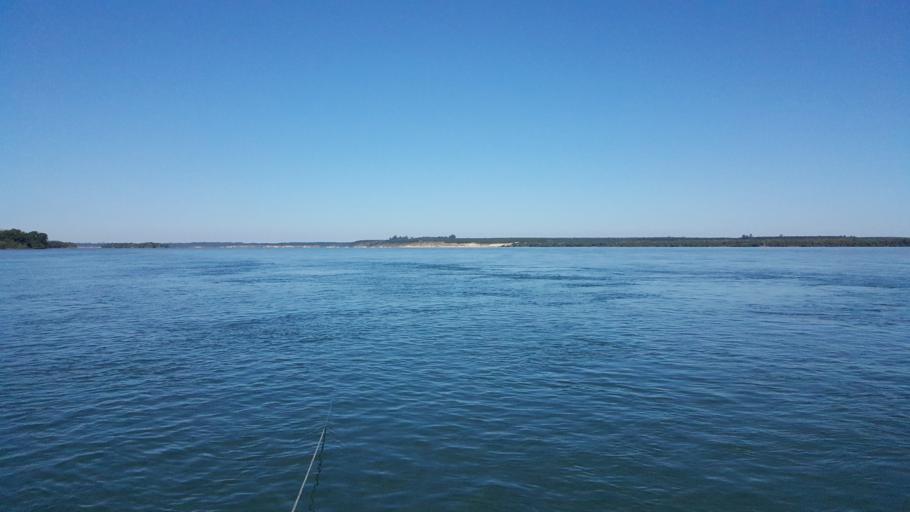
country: PY
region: Misiones
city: Ayolas
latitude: -27.5798
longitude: -56.8870
